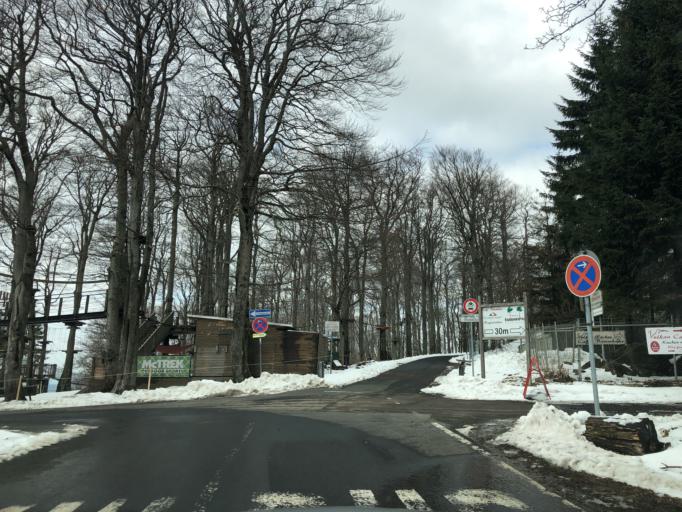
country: DE
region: Hesse
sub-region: Regierungsbezirk Giessen
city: Ulrichstein
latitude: 50.5104
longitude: 9.2267
